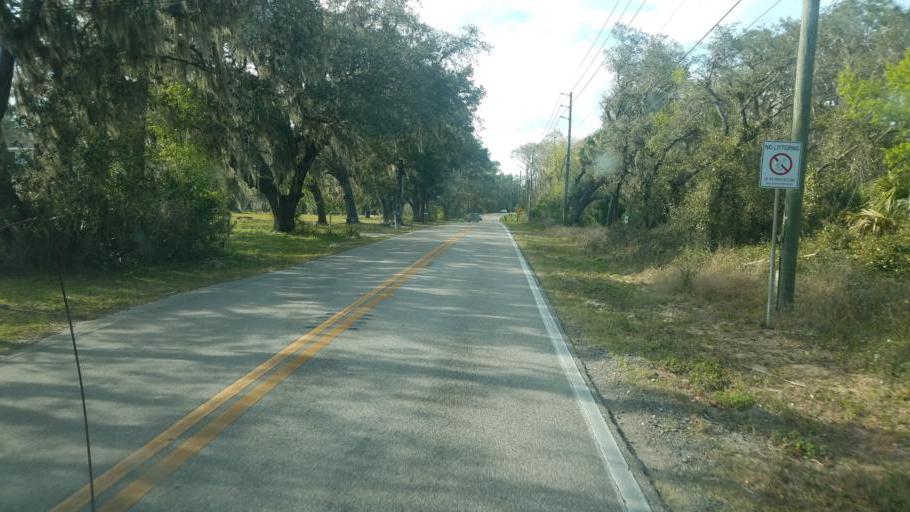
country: US
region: Florida
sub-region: Polk County
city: Loughman
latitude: 28.2545
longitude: -81.5752
